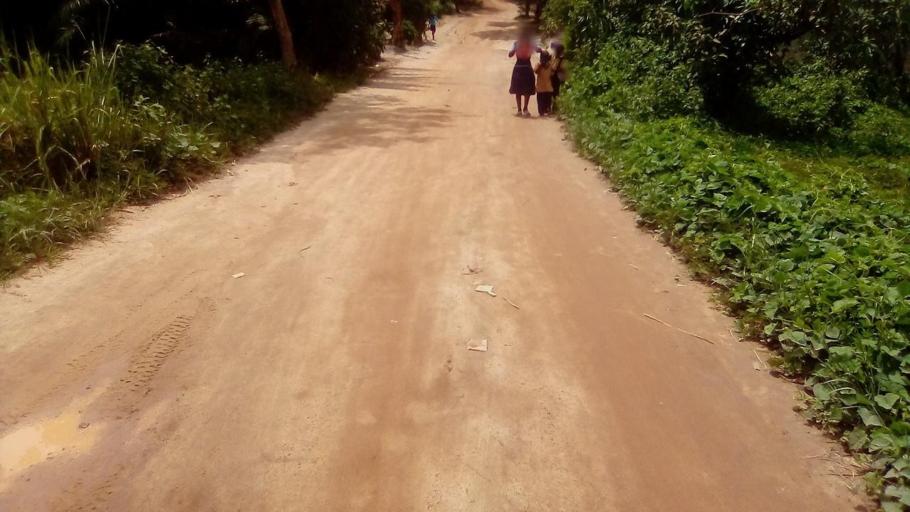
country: SL
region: Southern Province
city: Bo
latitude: 7.9413
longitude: -11.7363
